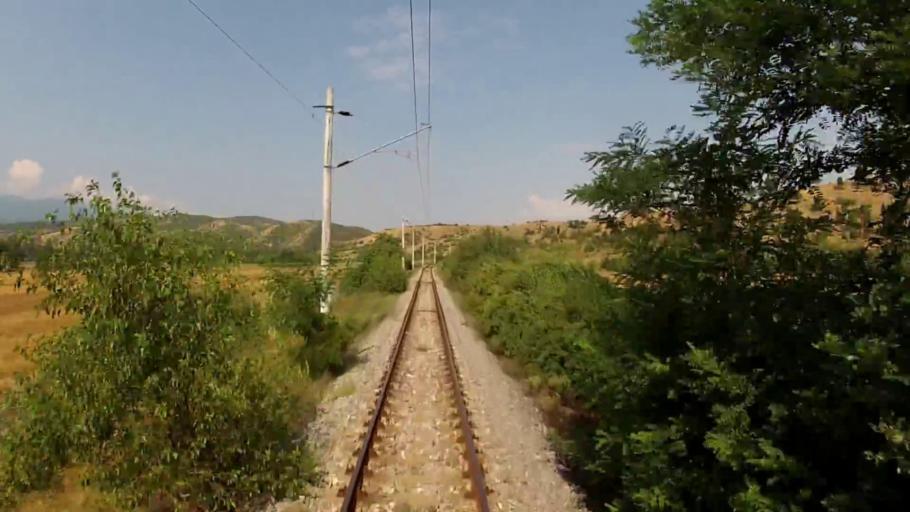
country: BG
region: Blagoevgrad
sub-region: Obshtina Petrich
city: Petrich
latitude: 41.4265
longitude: 23.3295
